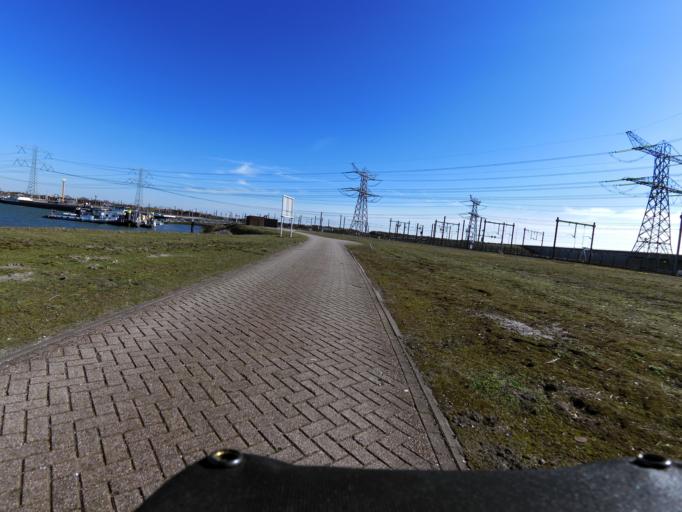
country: NL
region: South Holland
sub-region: Gemeente Rotterdam
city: Hoek van Holland
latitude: 51.9302
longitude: 4.0375
